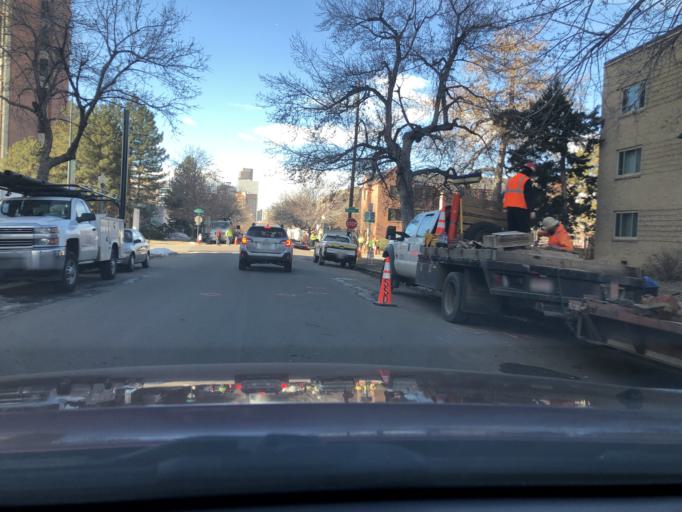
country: US
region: Colorado
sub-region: Denver County
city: Denver
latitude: 39.7482
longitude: -104.9678
